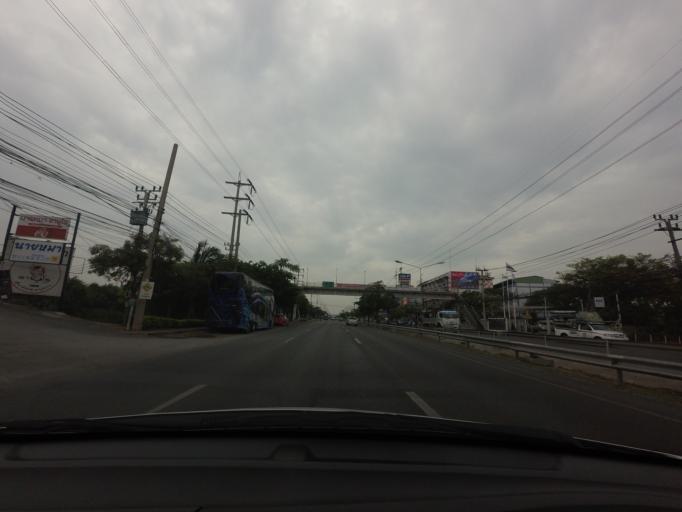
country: TH
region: Samut Prakan
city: Samut Prakan
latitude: 13.5379
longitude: 100.6232
